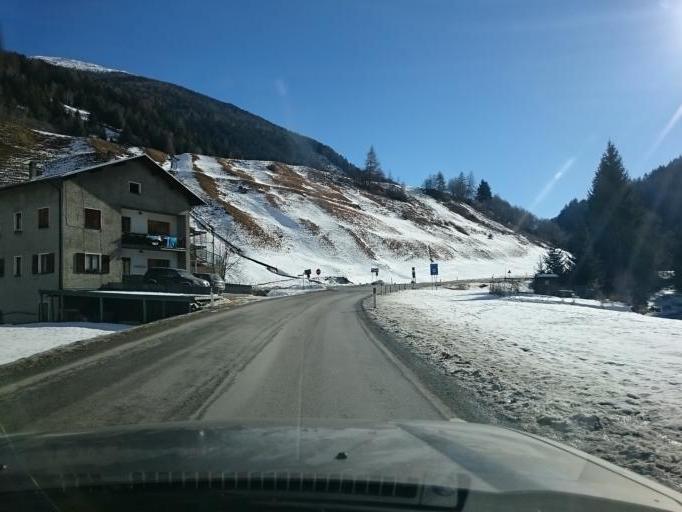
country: IT
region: Lombardy
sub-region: Provincia di Sondrio
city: Sant'Antonio
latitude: 46.4560
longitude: 10.4304
